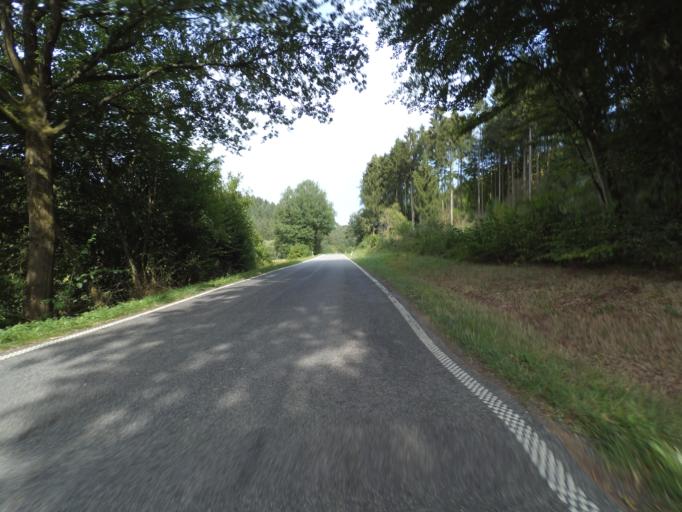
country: DE
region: Rheinland-Pfalz
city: Mannebach
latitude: 49.6477
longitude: 6.5115
